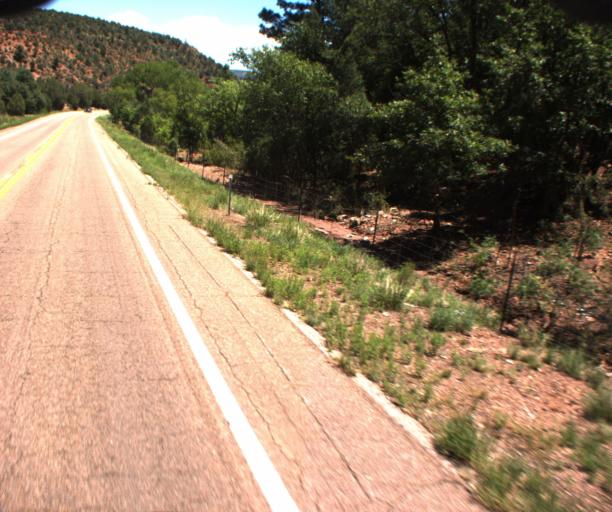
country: US
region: Arizona
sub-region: Navajo County
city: Cibecue
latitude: 33.9819
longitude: -110.3031
